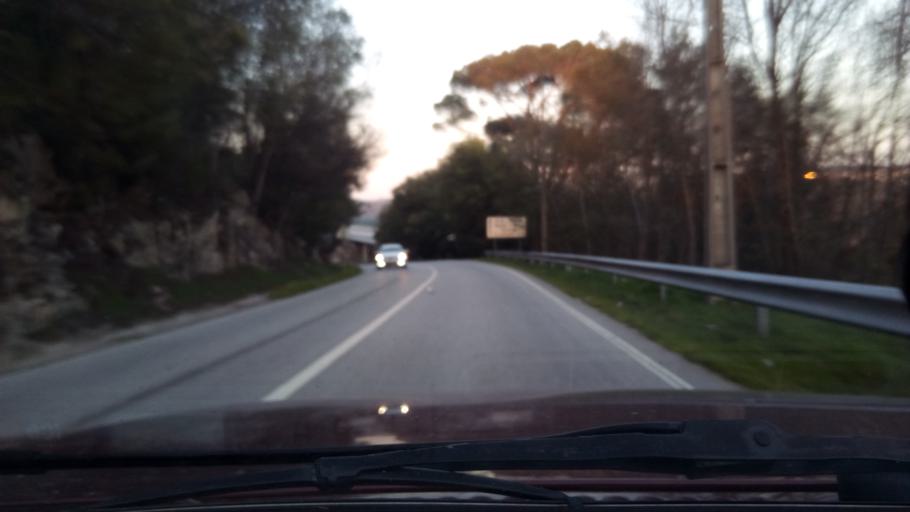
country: PT
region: Guarda
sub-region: Fornos de Algodres
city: Fornos de Algodres
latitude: 40.6094
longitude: -7.5323
